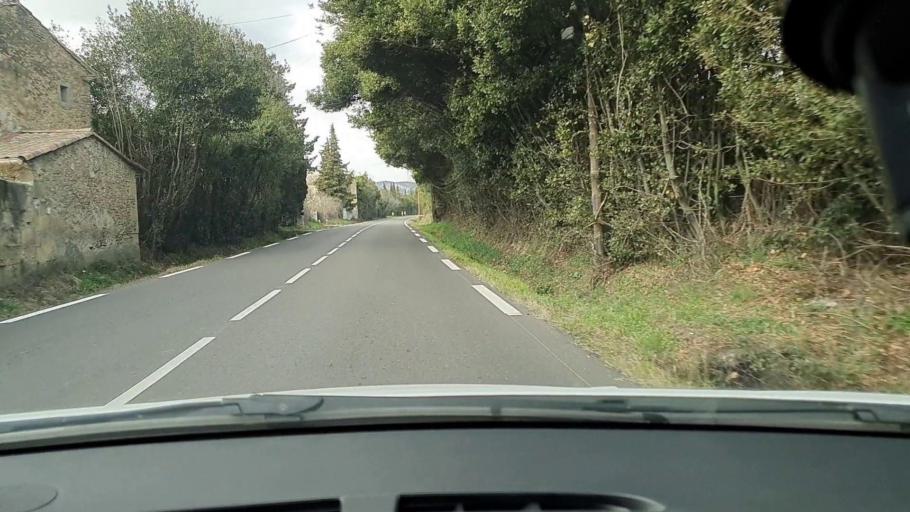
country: FR
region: Languedoc-Roussillon
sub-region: Departement du Gard
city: Sernhac
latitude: 43.9049
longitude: 4.5693
